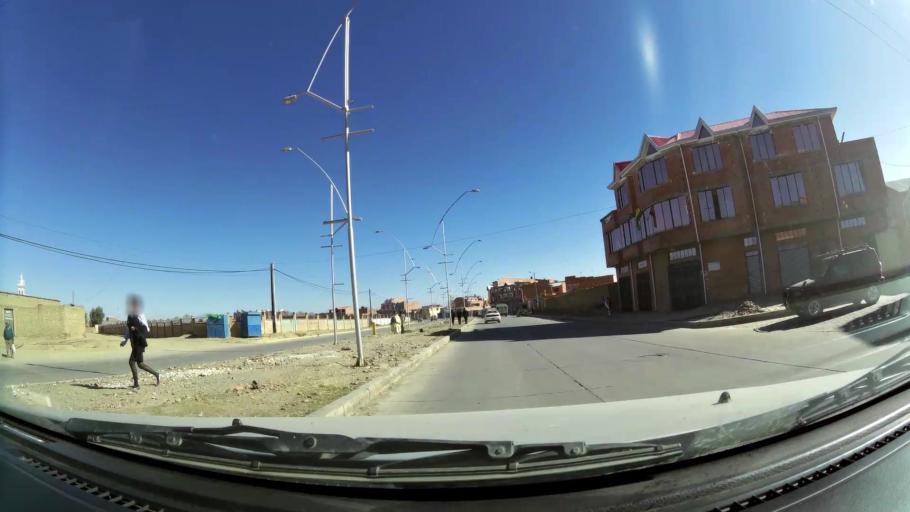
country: BO
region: La Paz
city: La Paz
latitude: -16.5270
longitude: -68.2216
